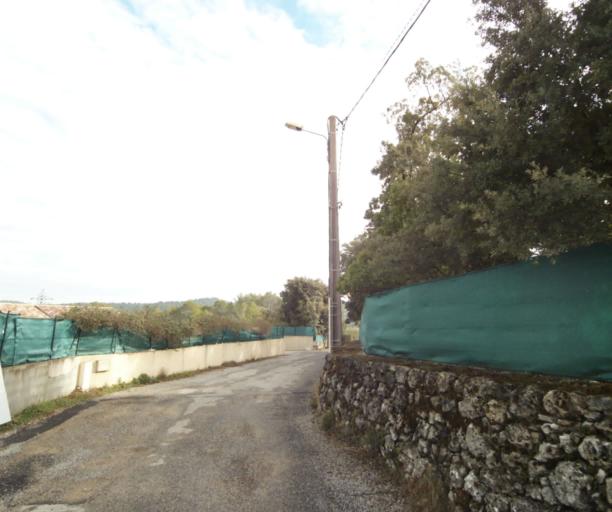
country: FR
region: Provence-Alpes-Cote d'Azur
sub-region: Departement du Var
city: Trans-en-Provence
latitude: 43.5040
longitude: 6.5027
